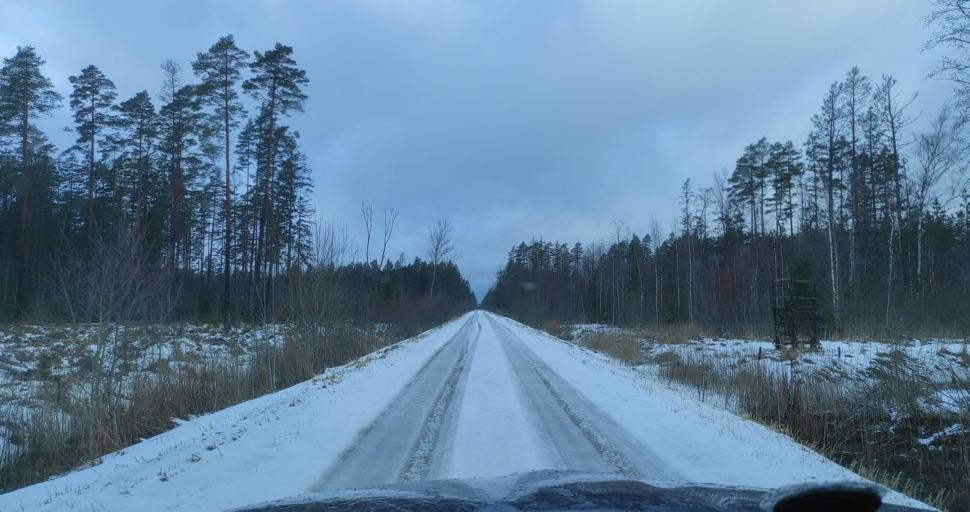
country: LV
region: Dundaga
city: Dundaga
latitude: 57.4055
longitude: 22.0952
